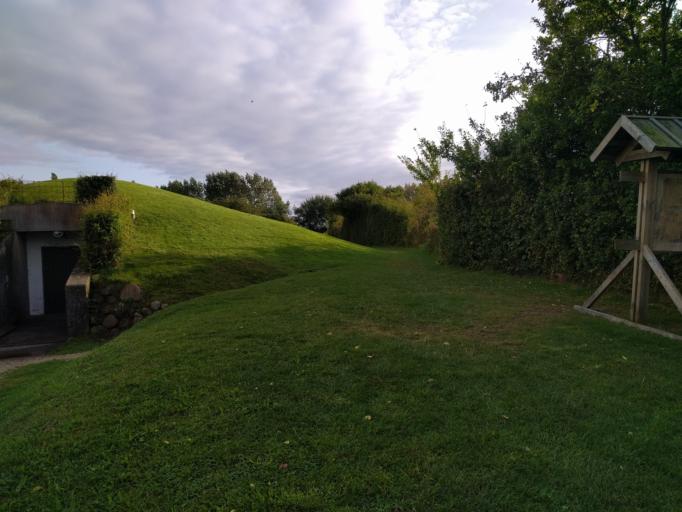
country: DK
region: South Denmark
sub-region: Kerteminde Kommune
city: Kerteminde
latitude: 55.4454
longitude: 10.6152
